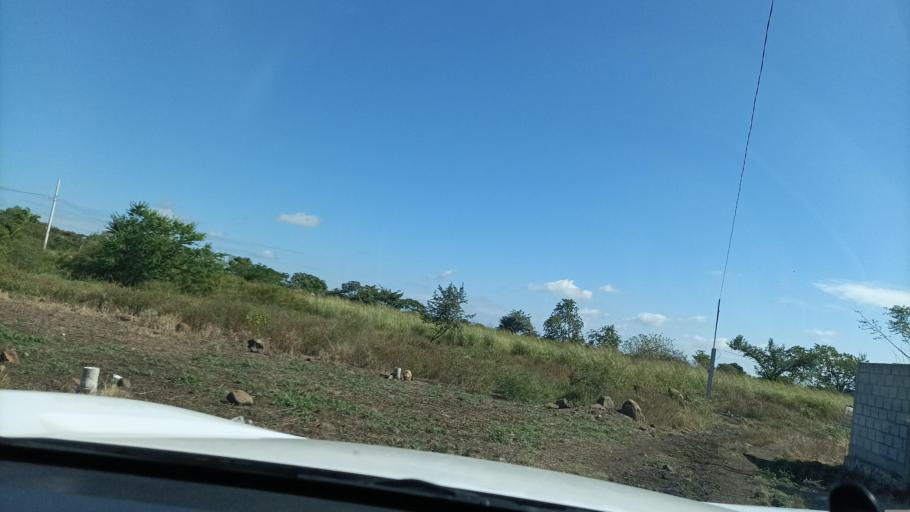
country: MX
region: Veracruz
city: Paso del Macho
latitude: 18.9607
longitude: -96.7237
